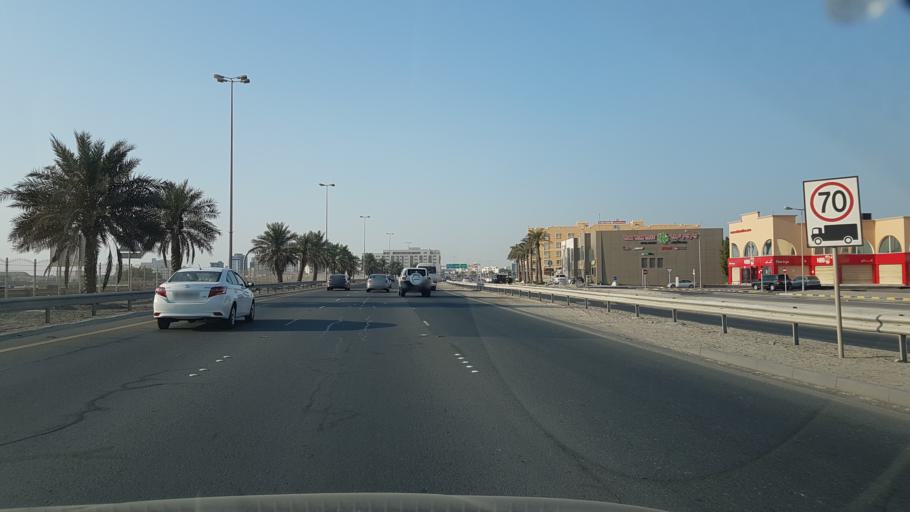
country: BH
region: Northern
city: Ar Rifa'
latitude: 26.1432
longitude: 50.5790
